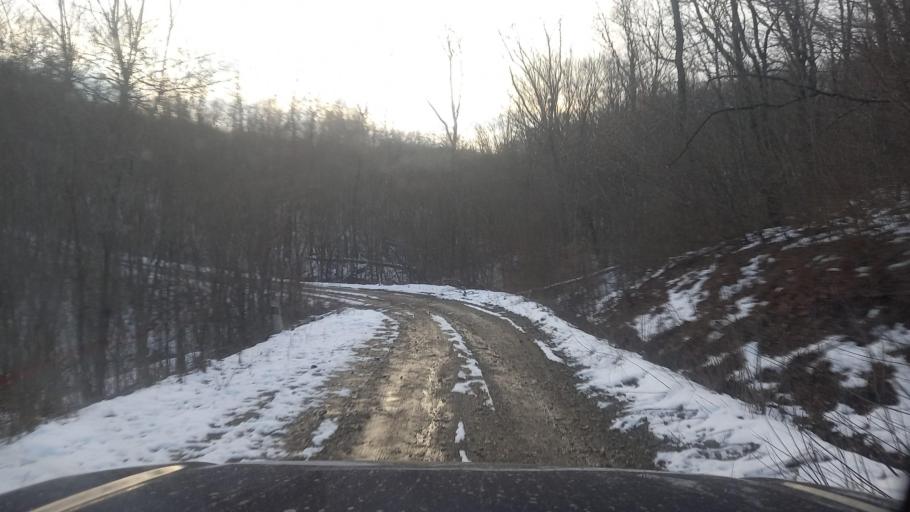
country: RU
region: Krasnodarskiy
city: Smolenskaya
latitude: 44.6816
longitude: 38.7788
